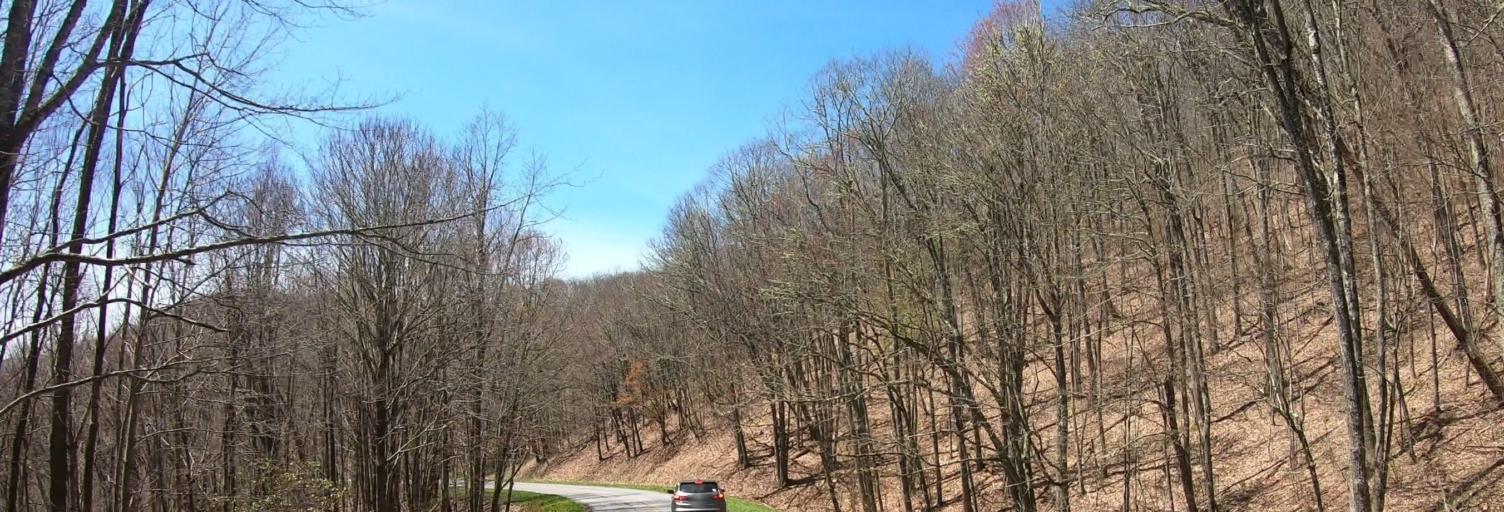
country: US
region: North Carolina
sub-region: Haywood County
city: Maggie Valley
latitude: 35.5105
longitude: -83.1589
